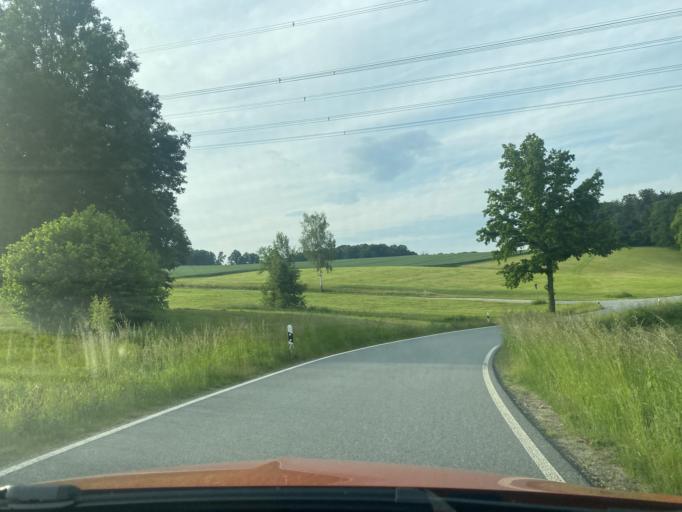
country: DE
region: Saxony
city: Bernstadt
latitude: 51.0311
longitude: 14.7993
